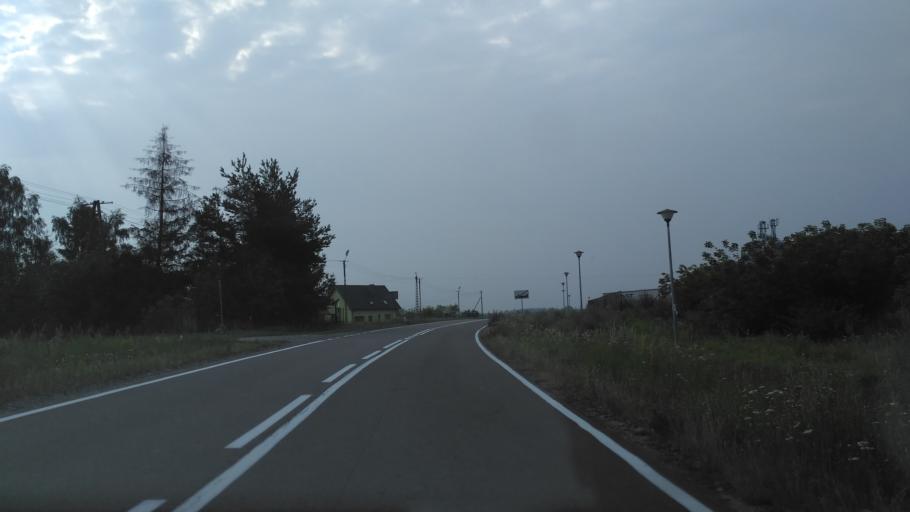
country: PL
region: Lublin Voivodeship
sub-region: Powiat chelmski
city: Rejowiec Fabryczny
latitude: 51.1852
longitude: 23.1717
